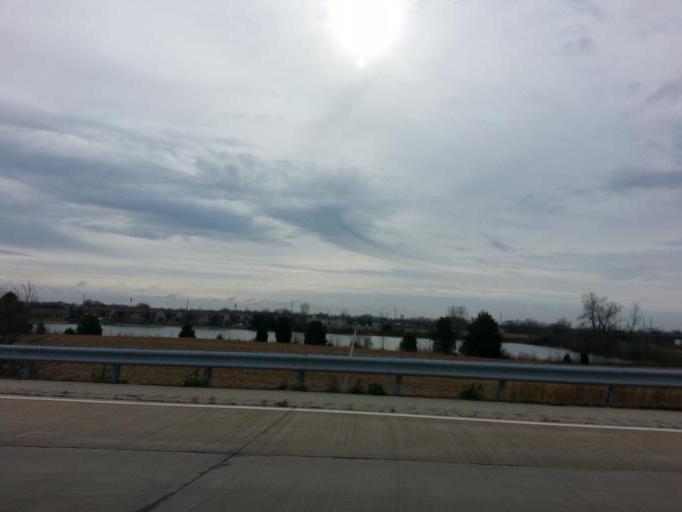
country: US
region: Indiana
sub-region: Decatur County
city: Greensburg
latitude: 39.3622
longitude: -85.4874
